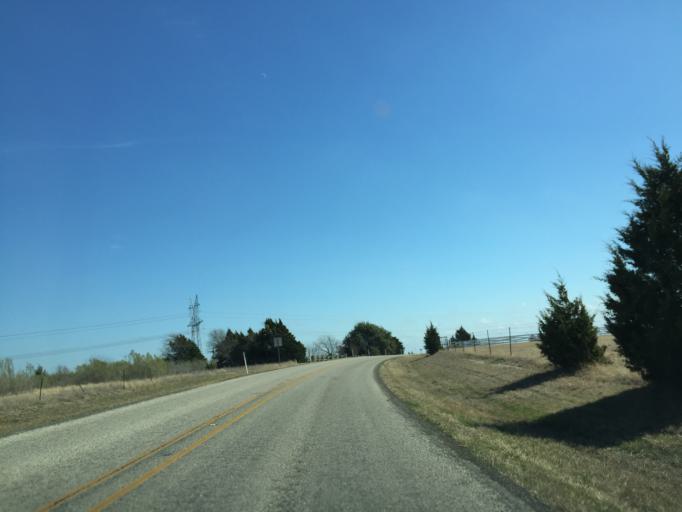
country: US
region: Texas
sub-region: Williamson County
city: Granger
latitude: 30.7587
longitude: -97.5275
